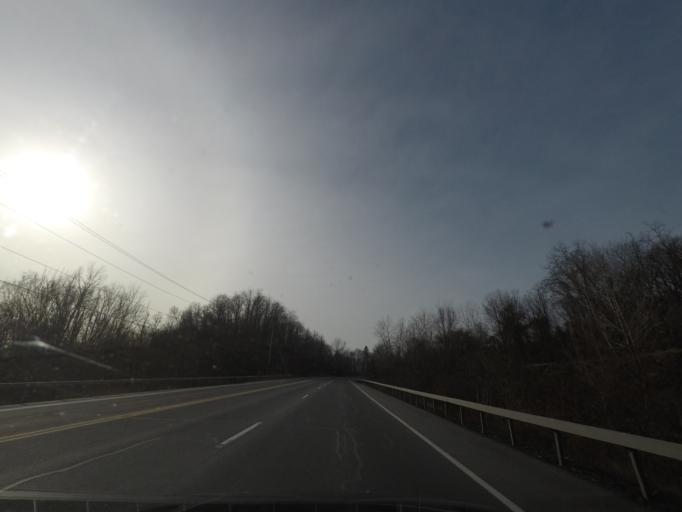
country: US
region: New York
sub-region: Saratoga County
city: Mechanicville
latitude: 42.8866
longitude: -73.6931
